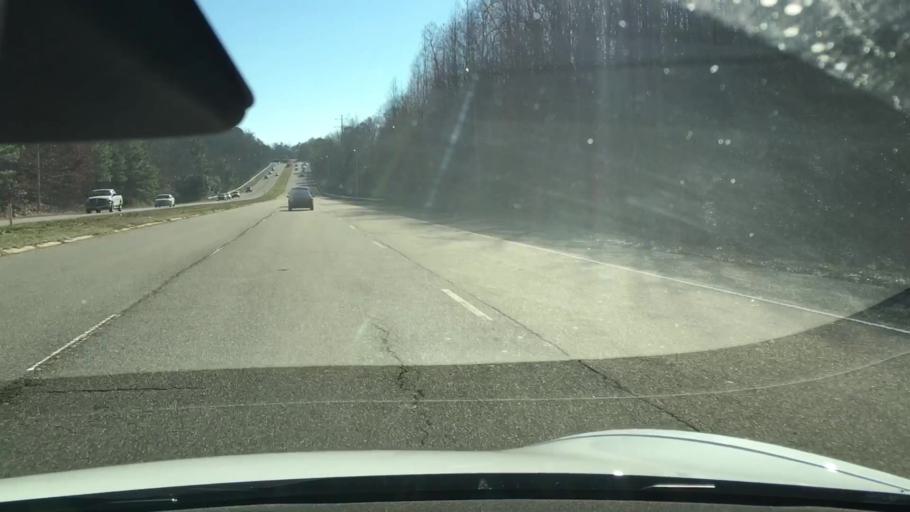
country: US
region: Virginia
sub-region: Chesterfield County
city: Bon Air
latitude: 37.5488
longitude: -77.5643
